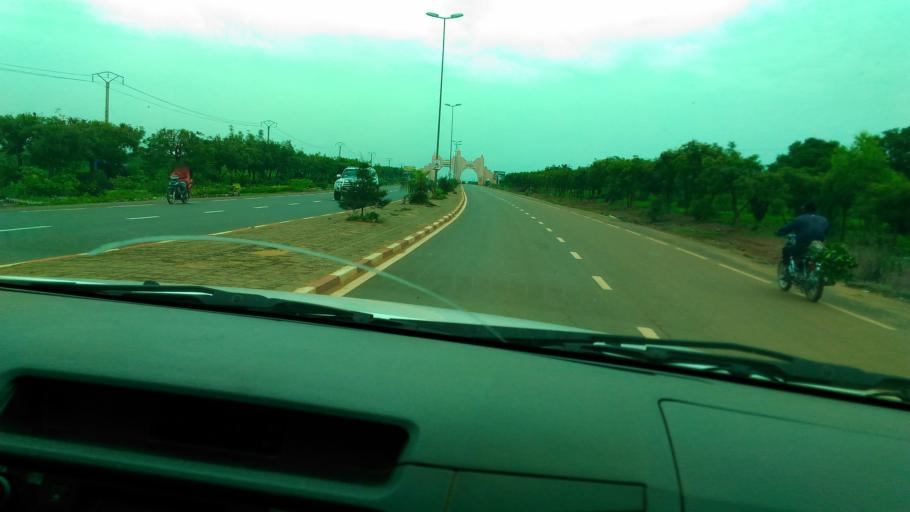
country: ML
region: Bamako
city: Bamako
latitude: 12.5574
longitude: -7.9770
